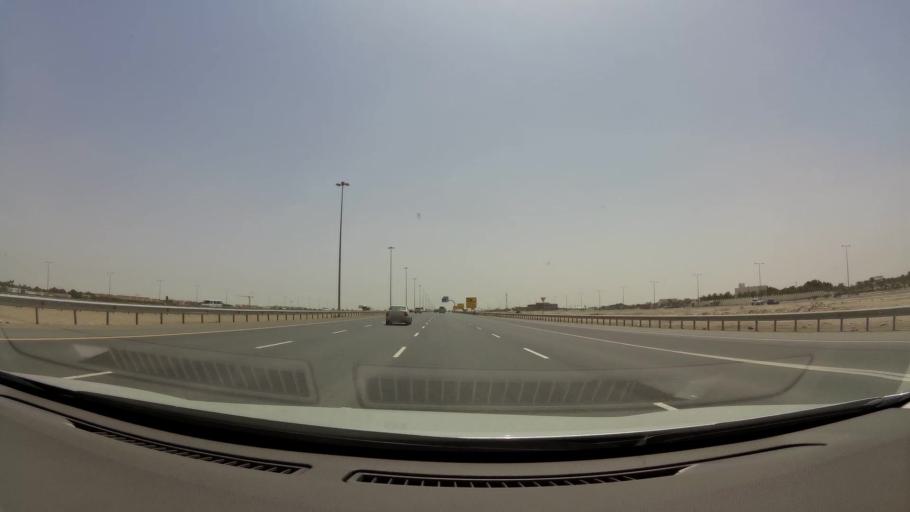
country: QA
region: Baladiyat Umm Salal
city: Umm Salal `Ali
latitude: 25.4654
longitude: 51.4083
